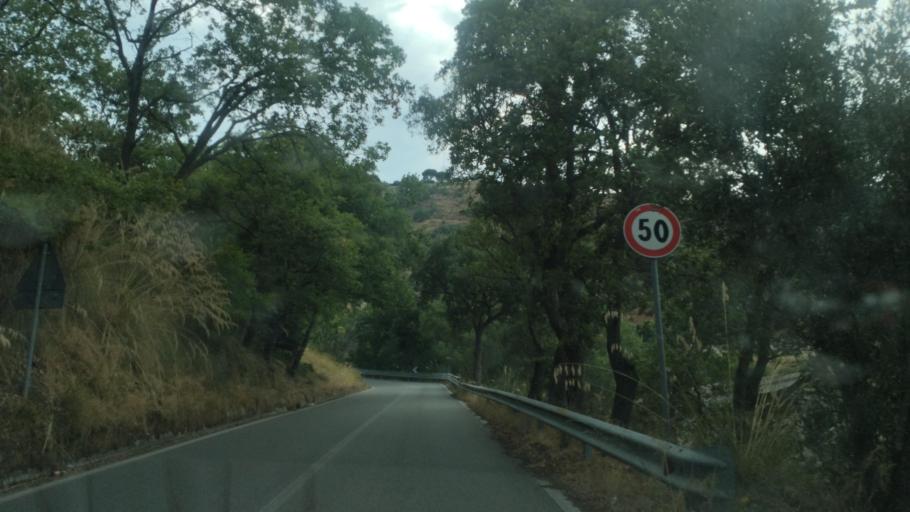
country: IT
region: Calabria
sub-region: Provincia di Catanzaro
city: Squillace Lido
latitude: 38.7605
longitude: 16.5650
